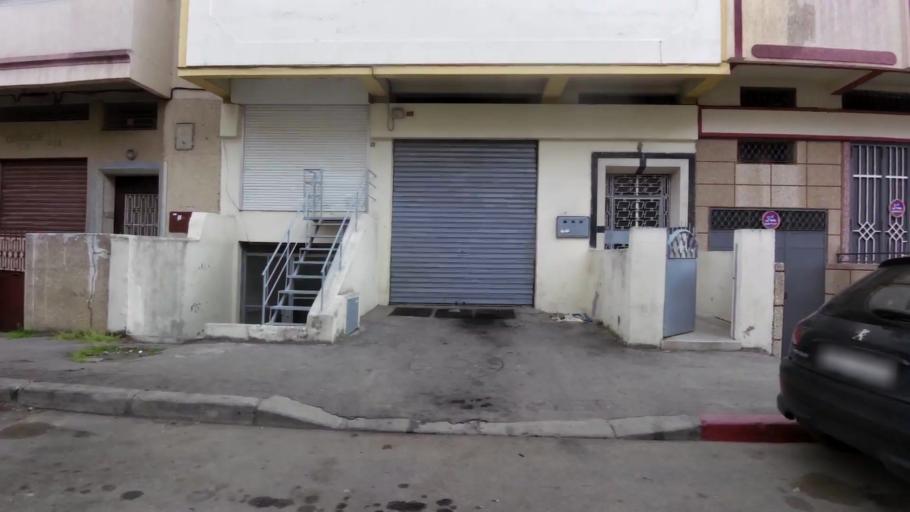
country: MA
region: Tanger-Tetouan
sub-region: Tanger-Assilah
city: Tangier
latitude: 35.7687
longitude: -5.8176
